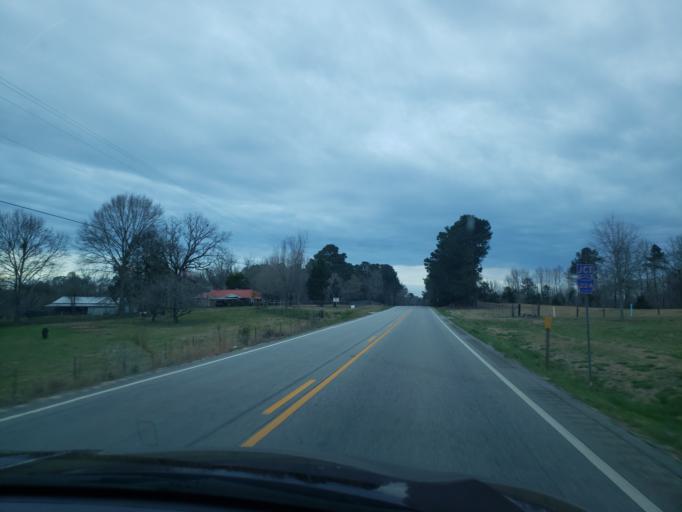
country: US
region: Alabama
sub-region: Chambers County
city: Lafayette
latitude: 32.9676
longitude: -85.4034
